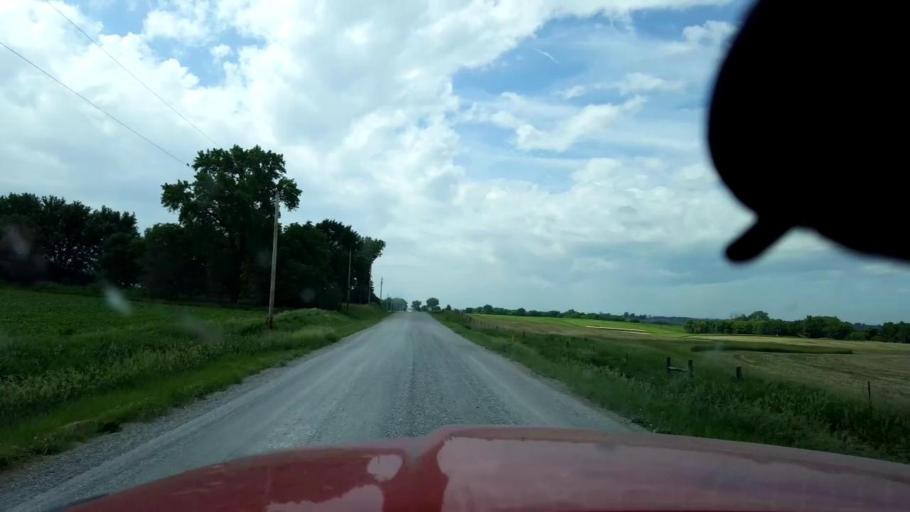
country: US
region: Iowa
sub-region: Cherokee County
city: Cherokee
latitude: 42.8190
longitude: -95.5346
